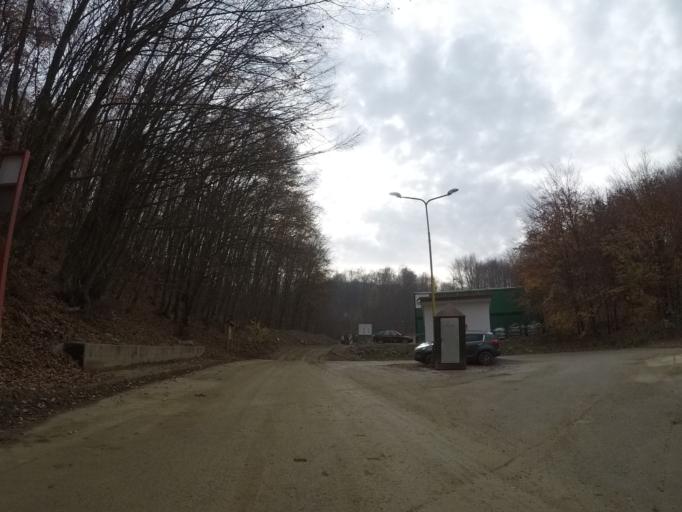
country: SK
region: Presovsky
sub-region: Okres Presov
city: Presov
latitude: 48.9813
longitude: 21.2172
